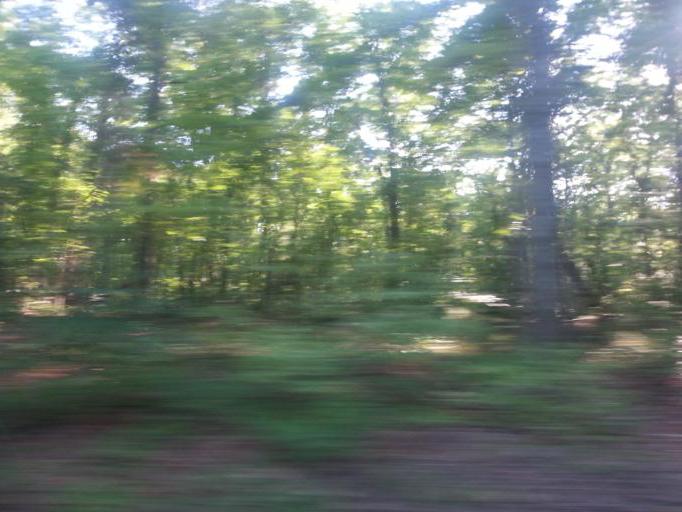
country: US
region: Tennessee
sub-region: Blount County
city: Maryville
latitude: 35.6429
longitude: -83.9551
